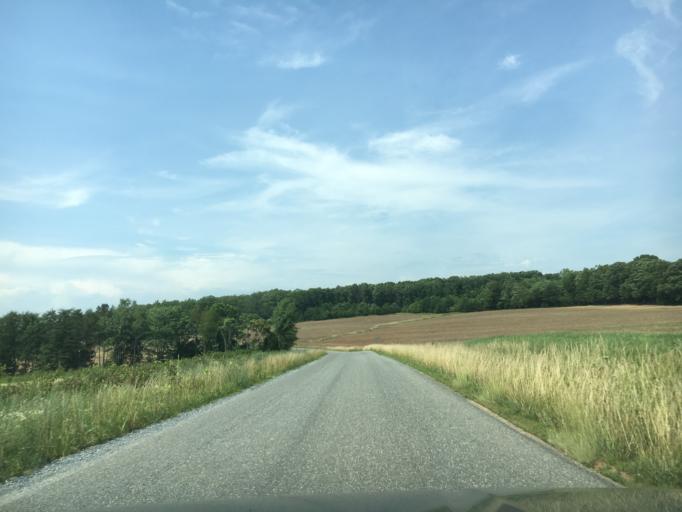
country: US
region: Virginia
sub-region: Pittsylvania County
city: Gretna
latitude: 36.8997
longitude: -79.4072
